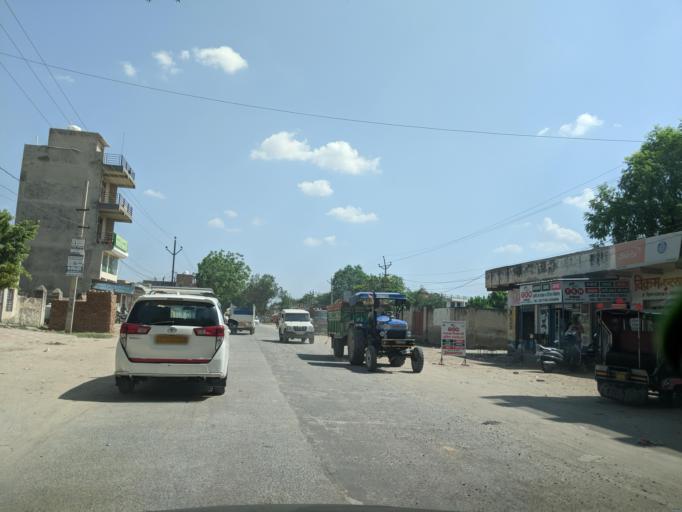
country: IN
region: Rajasthan
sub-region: Jhunjhunun
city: Jhunjhunun
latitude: 28.1372
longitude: 75.3851
